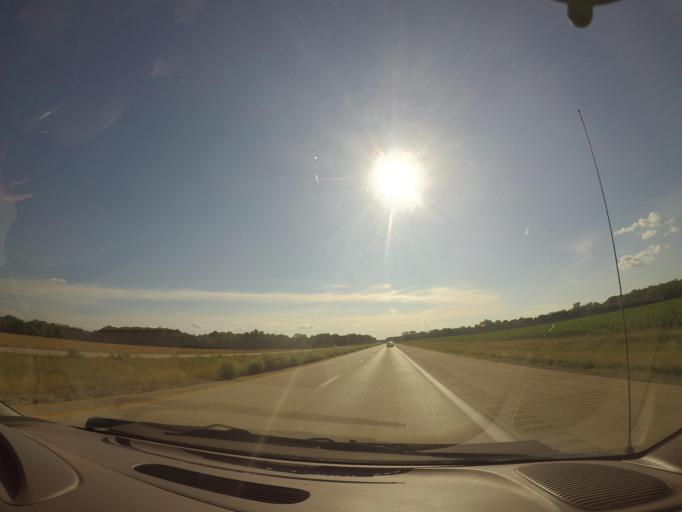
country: US
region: Ohio
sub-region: Henry County
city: Liberty Center
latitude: 41.4332
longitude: -83.9463
